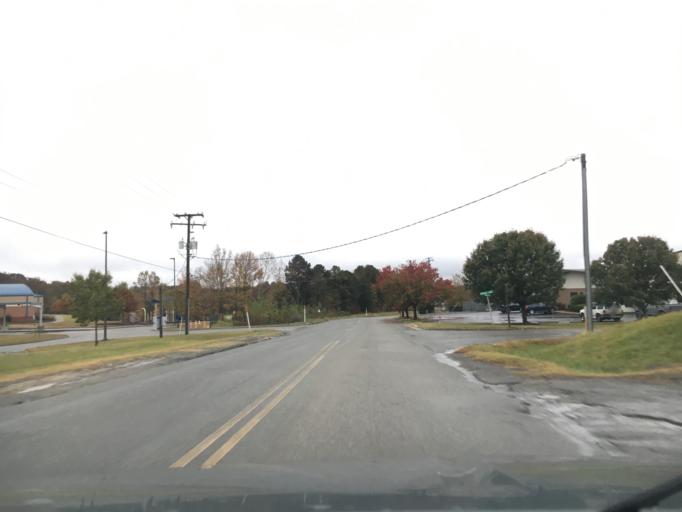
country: US
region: Virginia
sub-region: Halifax County
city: South Boston
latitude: 36.7196
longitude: -78.8915
